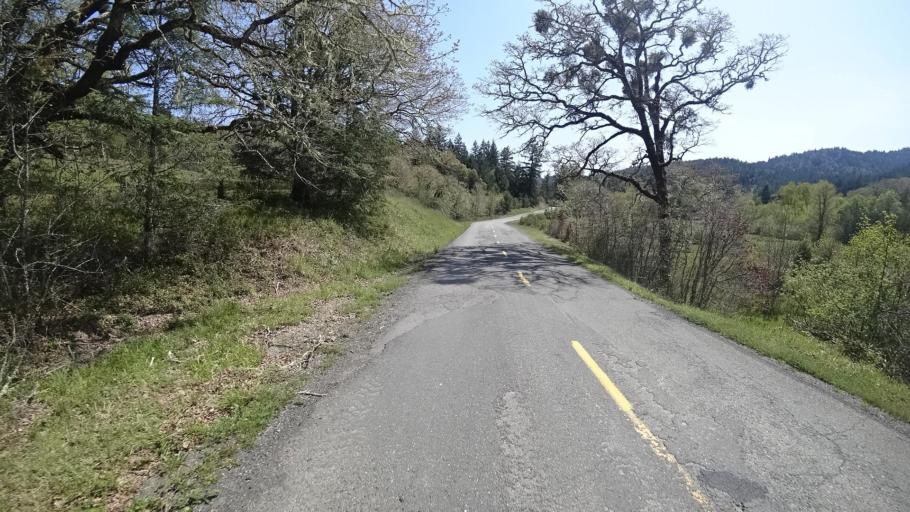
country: US
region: California
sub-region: Humboldt County
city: Redway
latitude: 40.3036
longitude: -123.6542
